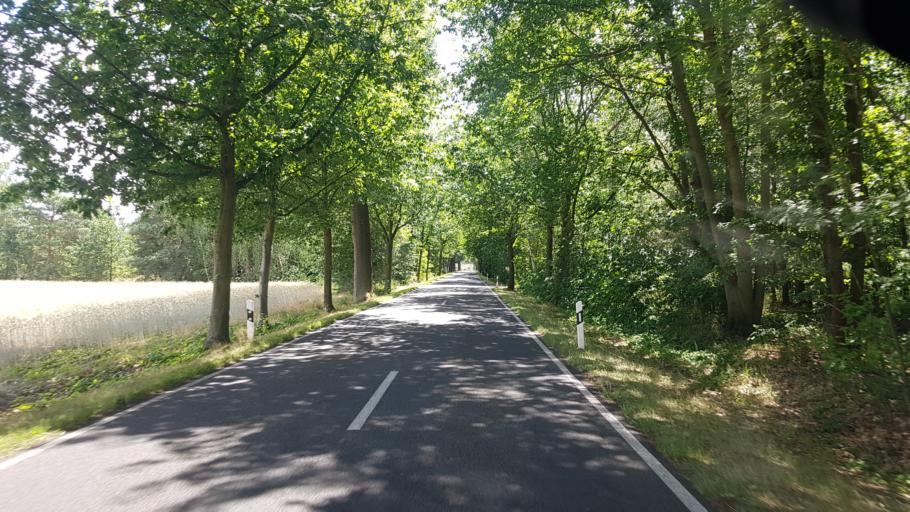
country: DE
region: Brandenburg
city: Sallgast
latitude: 51.5958
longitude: 13.8458
